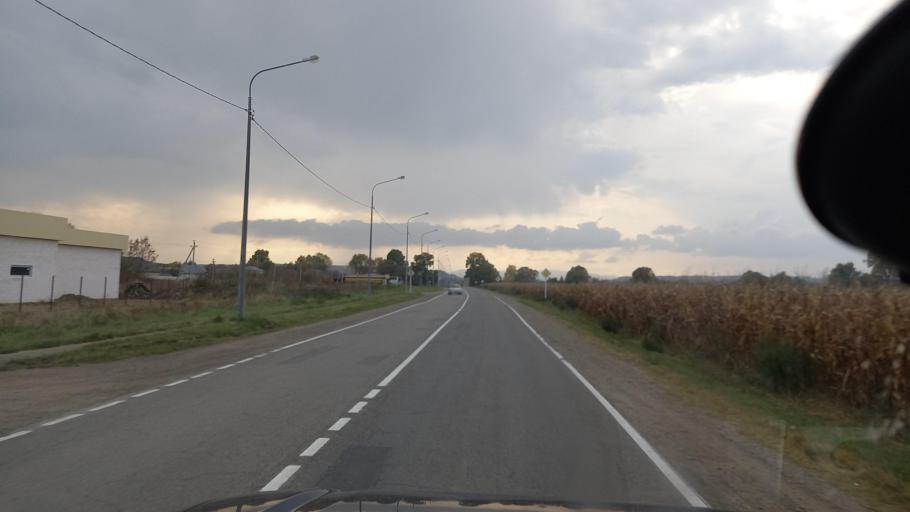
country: RU
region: Krasnodarskiy
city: Mostovskoy
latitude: 44.3983
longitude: 40.7747
